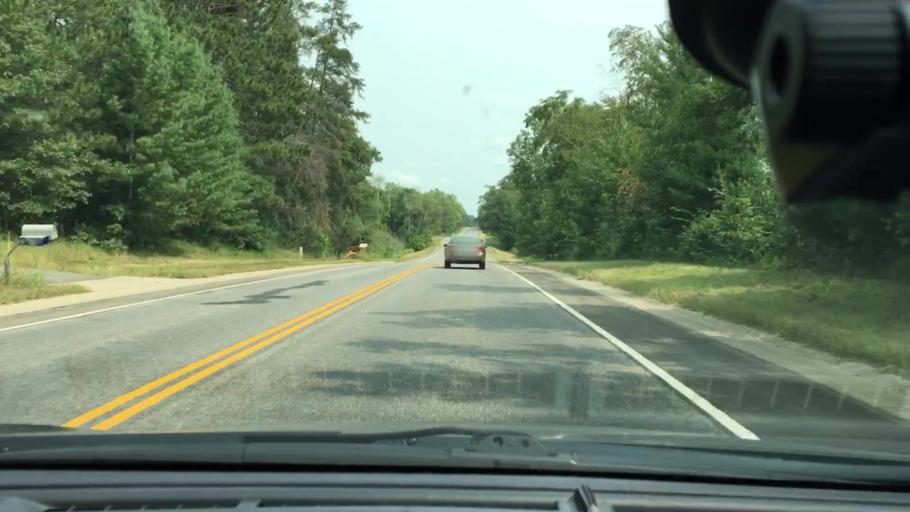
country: US
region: Minnesota
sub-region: Cass County
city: East Gull Lake
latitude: 46.4128
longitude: -94.3237
